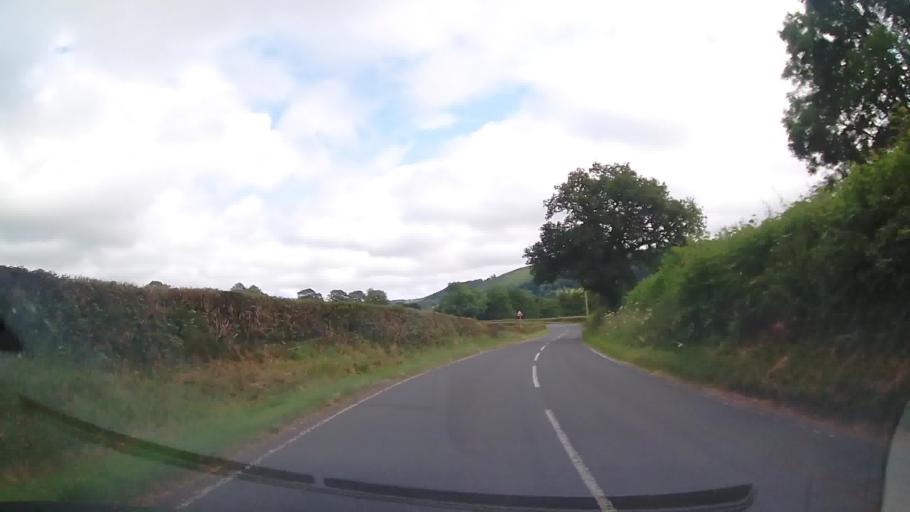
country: GB
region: Wales
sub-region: Sir Powys
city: Llanrhaeadr-ym-Mochnant
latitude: 52.8151
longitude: -3.2746
